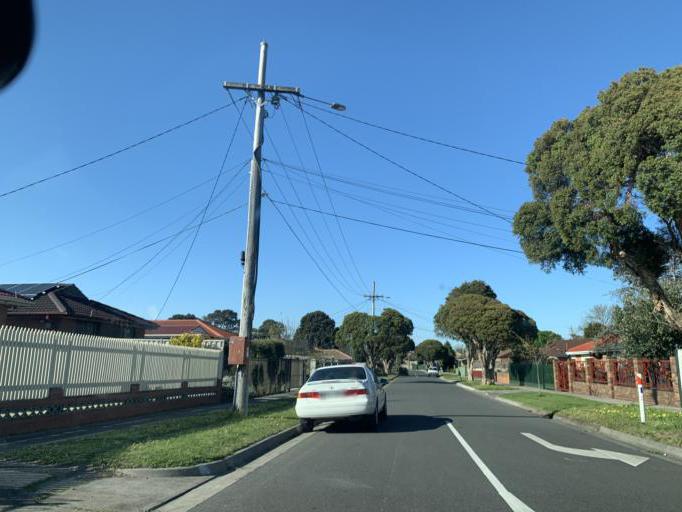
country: AU
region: Victoria
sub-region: Greater Dandenong
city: Keysborough
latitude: -37.9865
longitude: 145.1854
